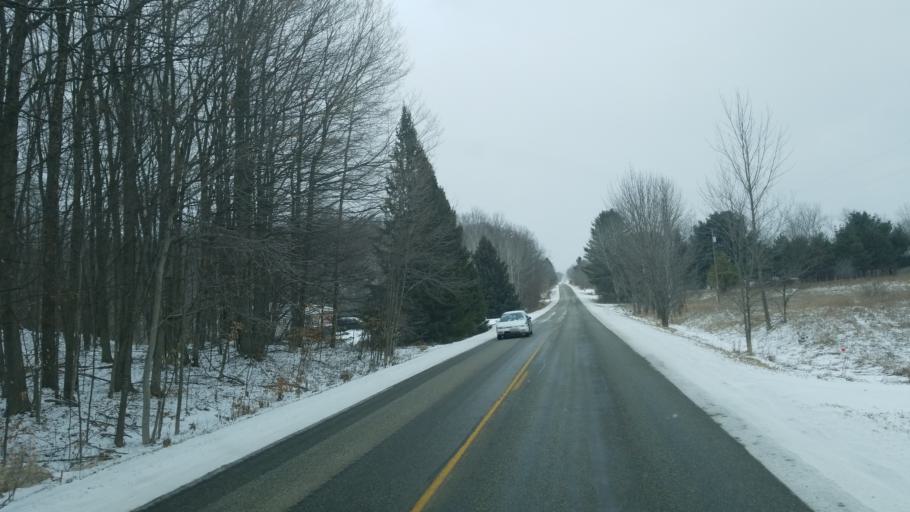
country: US
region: Michigan
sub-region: Osceola County
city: Evart
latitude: 43.9848
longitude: -85.2465
